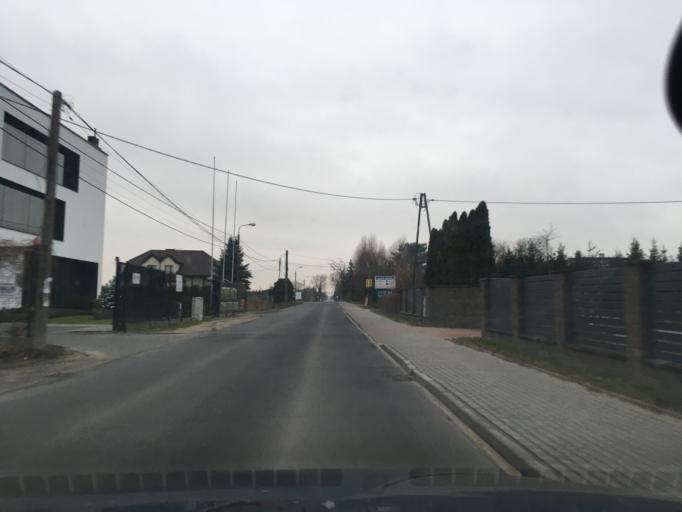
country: PL
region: Masovian Voivodeship
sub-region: Powiat piaseczynski
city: Mysiadlo
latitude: 52.1271
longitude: 20.9797
